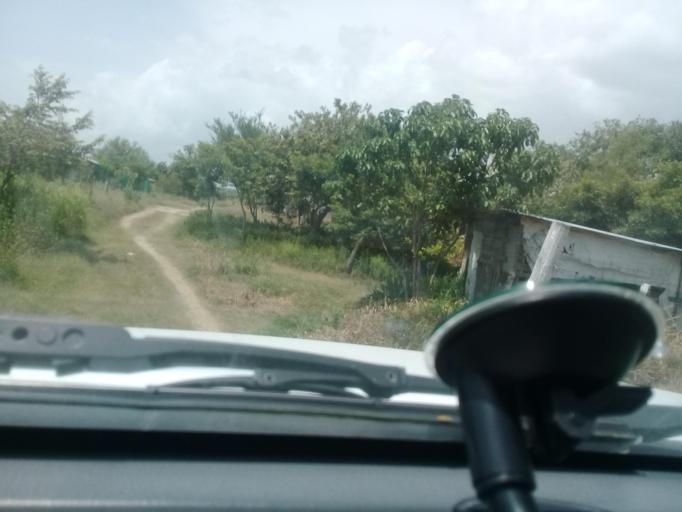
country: MX
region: Veracruz
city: Anahuac
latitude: 22.2266
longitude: -97.8259
